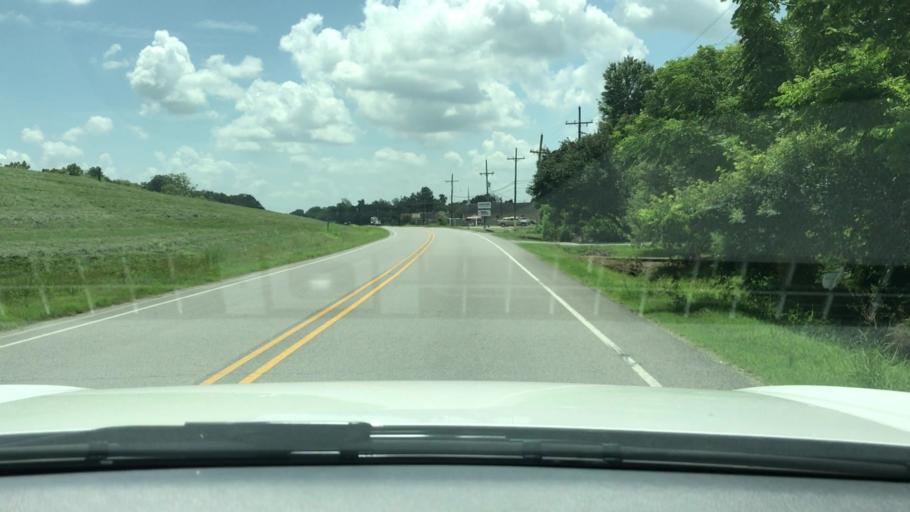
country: US
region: Louisiana
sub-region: Iberville Parish
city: Plaquemine
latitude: 30.2815
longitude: -91.2230
